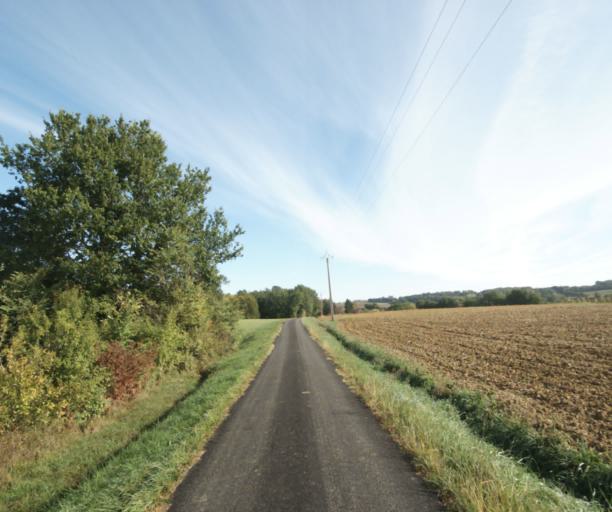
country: FR
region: Midi-Pyrenees
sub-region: Departement du Gers
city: Montreal
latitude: 43.9451
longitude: 0.1311
